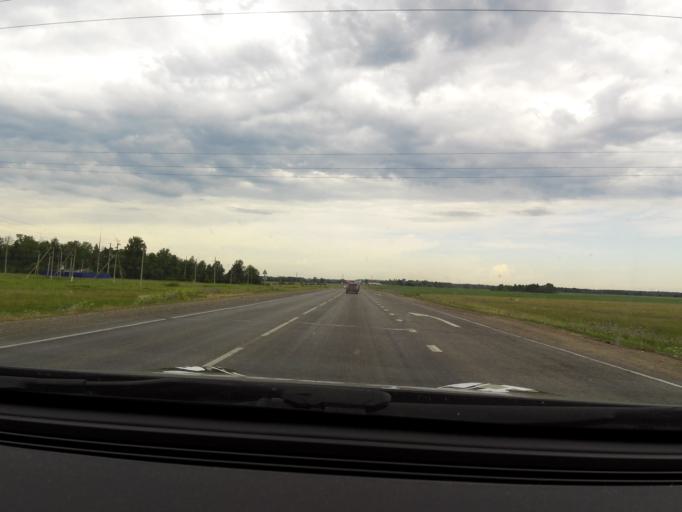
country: RU
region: Bashkortostan
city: Kudeyevskiy
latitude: 54.8169
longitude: 56.7538
